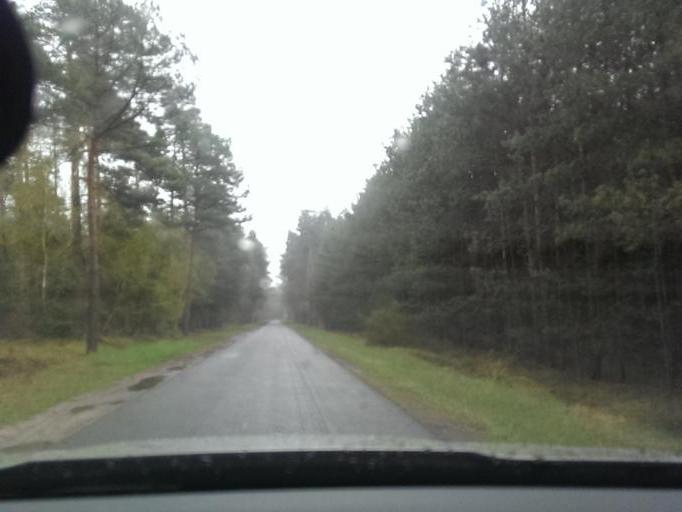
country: DE
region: Lower Saxony
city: Elze
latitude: 52.5954
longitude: 9.7781
